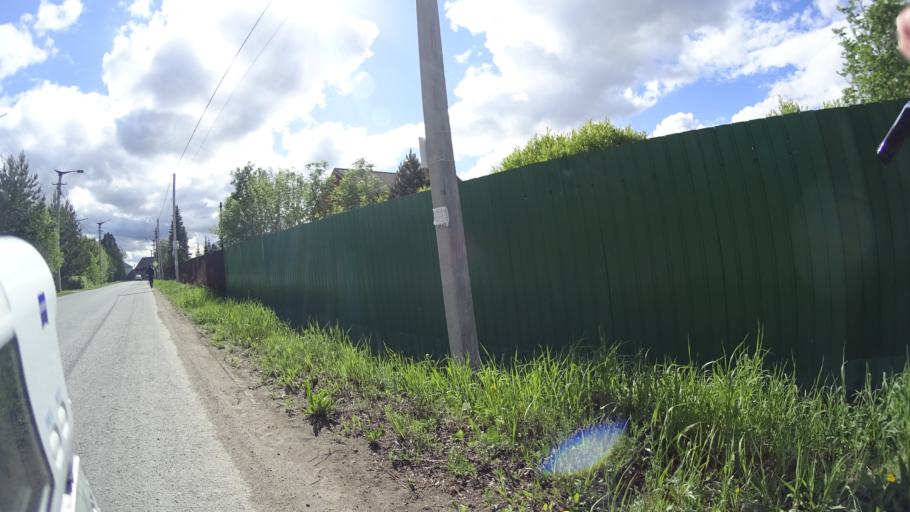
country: RU
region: Chelyabinsk
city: Sargazy
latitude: 55.1447
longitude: 61.2326
